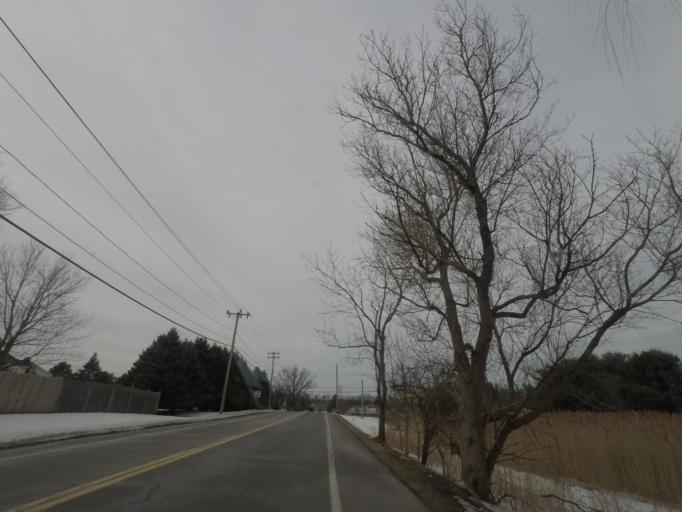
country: US
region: New York
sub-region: Albany County
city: Westmere
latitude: 42.6819
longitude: -73.9017
